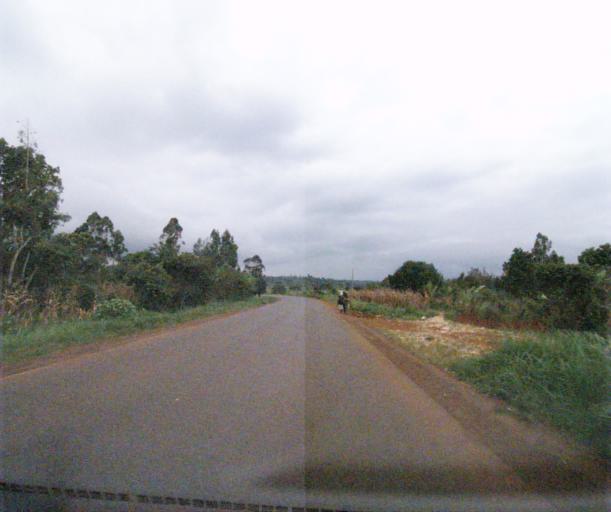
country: CM
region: West
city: Bansoa
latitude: 5.4853
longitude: 10.2175
